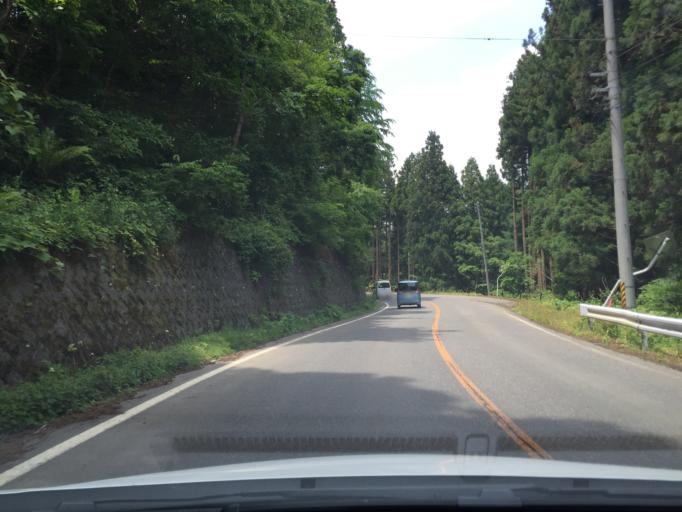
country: JP
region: Fukushima
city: Inawashiro
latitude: 37.6195
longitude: 140.1148
